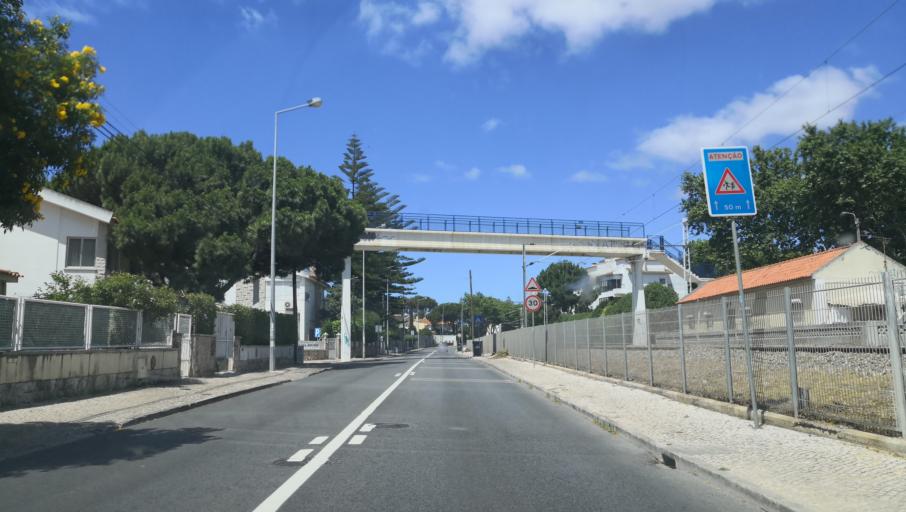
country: PT
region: Lisbon
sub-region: Cascais
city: Parede
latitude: 38.6874
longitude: -9.3471
